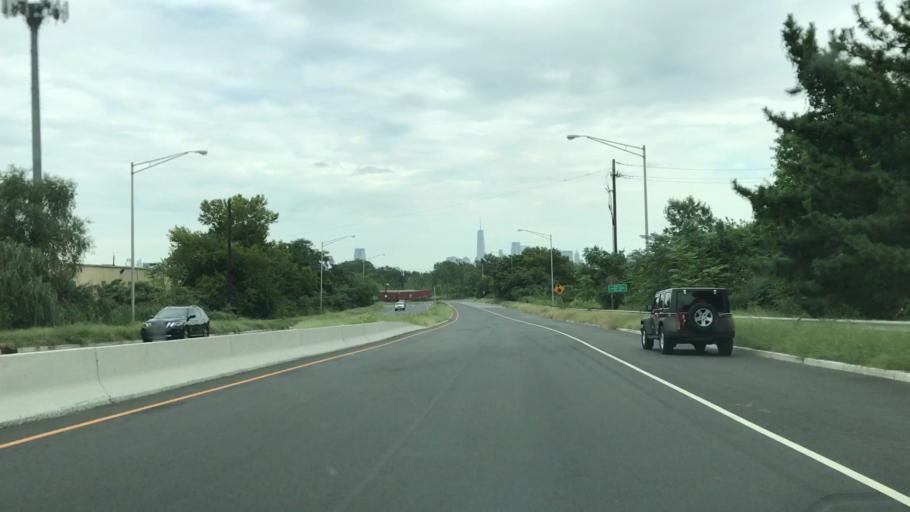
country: US
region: New Jersey
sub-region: Hudson County
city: Bayonne
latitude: 40.6877
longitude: -74.0865
